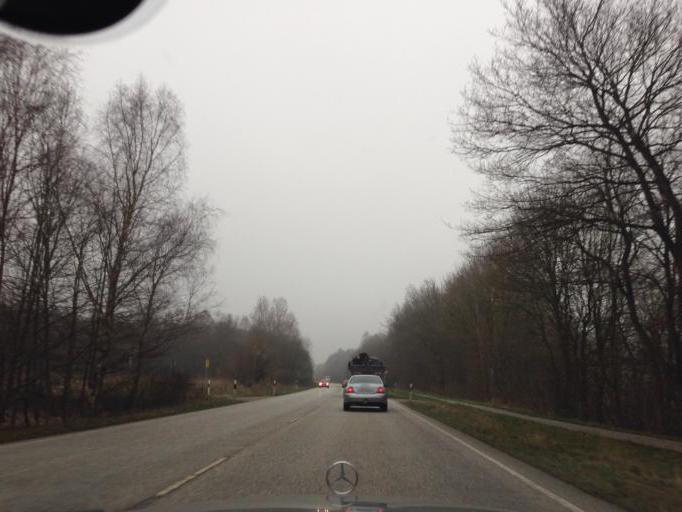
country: DE
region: Schleswig-Holstein
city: Klein Barkau
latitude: 54.2569
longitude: 10.1484
